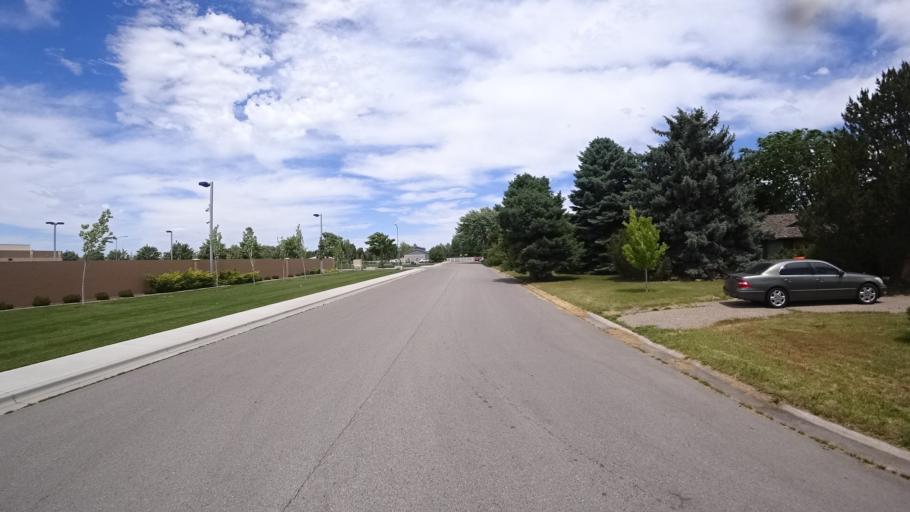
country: US
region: Idaho
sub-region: Ada County
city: Meridian
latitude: 43.6210
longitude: -116.3420
